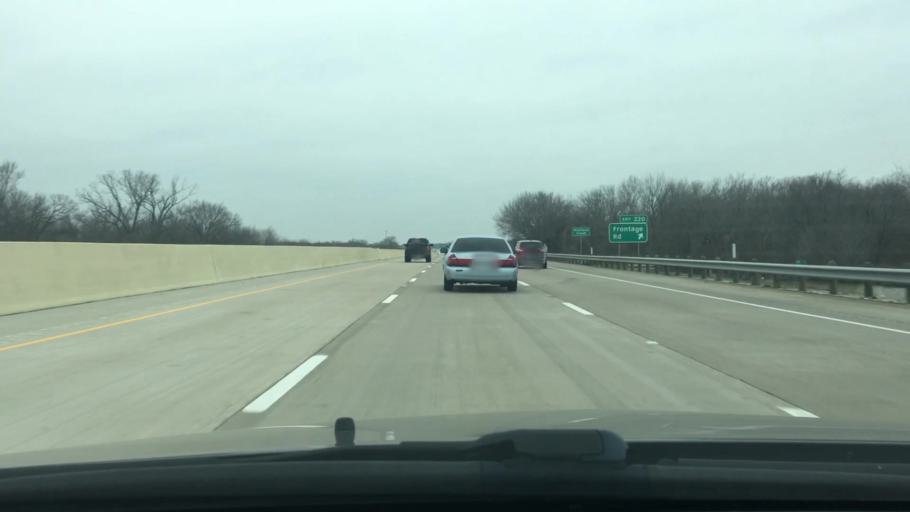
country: US
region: Texas
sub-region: Navarro County
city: Corsicana
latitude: 31.9514
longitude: -96.4216
